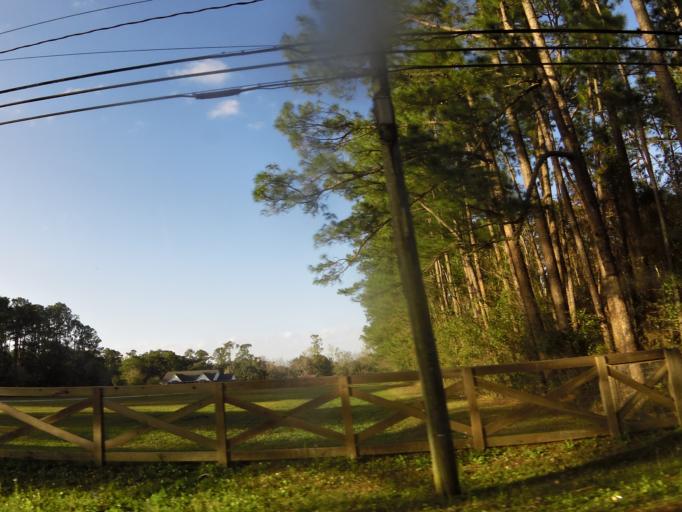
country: US
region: Florida
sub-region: Duval County
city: Jacksonville
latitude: 30.2680
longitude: -81.5786
